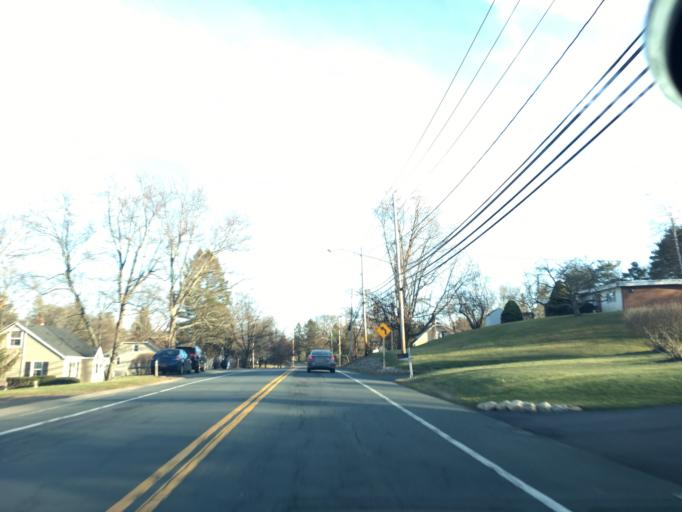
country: US
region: New York
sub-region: Rensselaer County
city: Wynantskill
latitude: 42.6926
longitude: -73.6515
